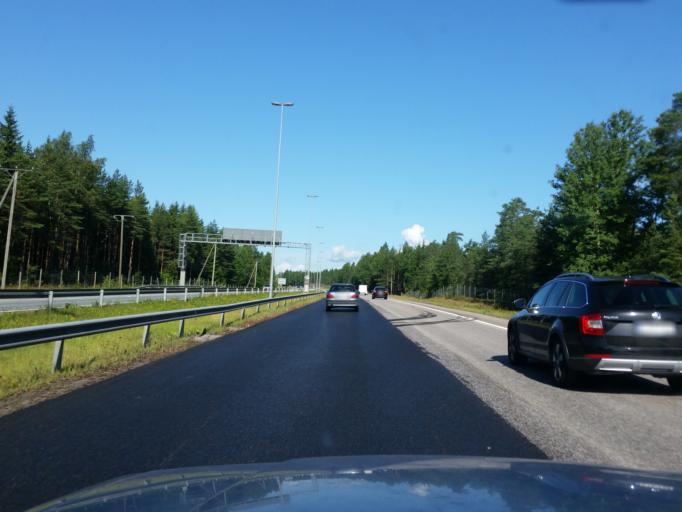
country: FI
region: Uusimaa
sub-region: Helsinki
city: Espoo
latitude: 60.2522
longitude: 24.5298
